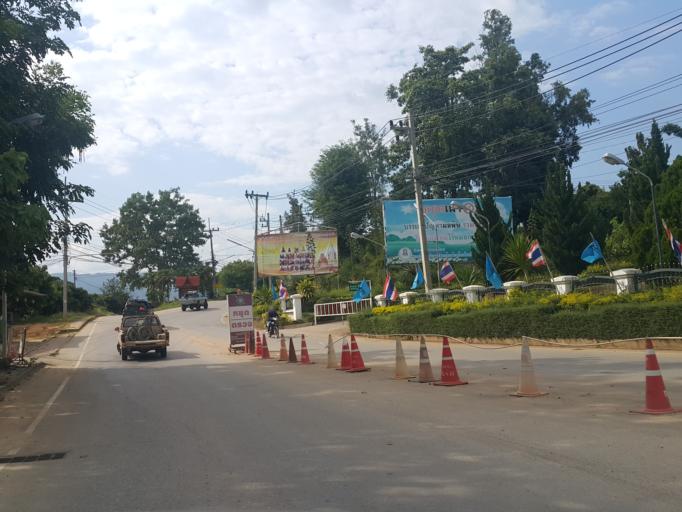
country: TH
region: Chiang Mai
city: Mae Chaem
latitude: 18.4958
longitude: 98.3730
